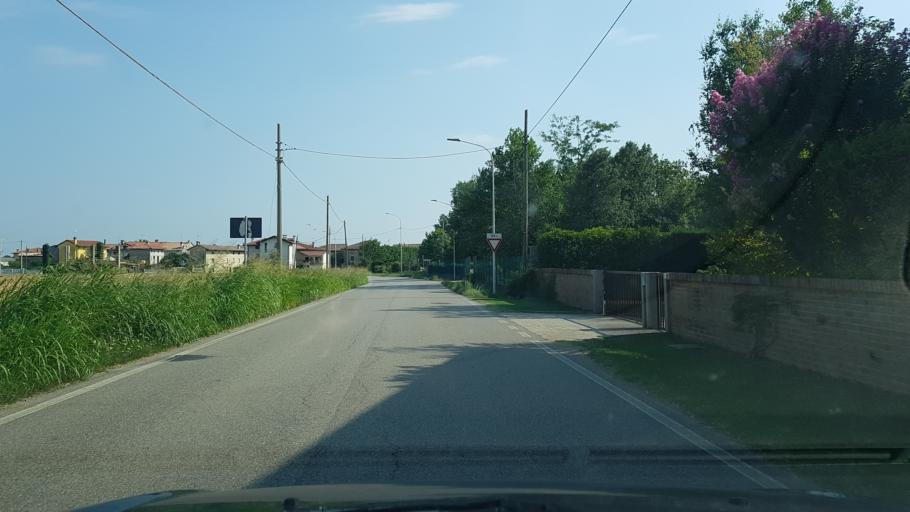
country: IT
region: Friuli Venezia Giulia
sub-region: Provincia di Udine
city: San Vito di Fagagna
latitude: 46.0705
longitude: 13.0804
